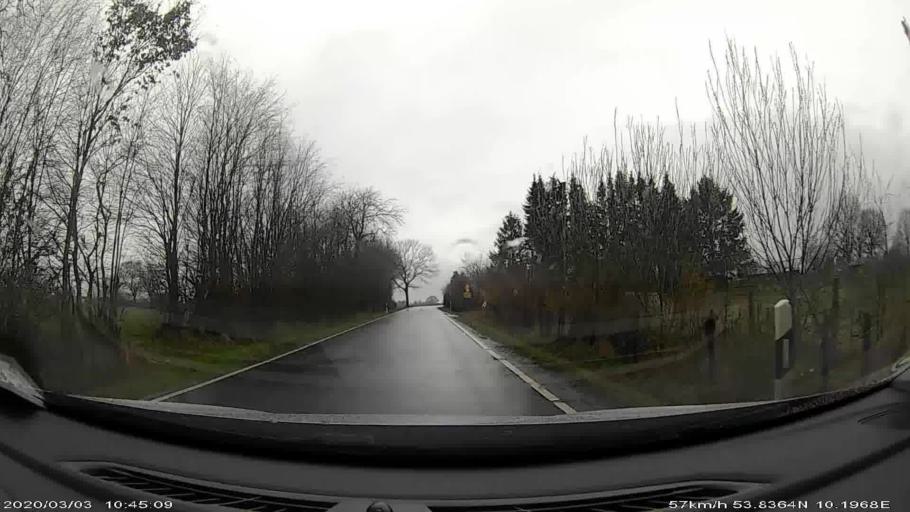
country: DE
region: Schleswig-Holstein
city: Seth
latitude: 53.8382
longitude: 10.1940
